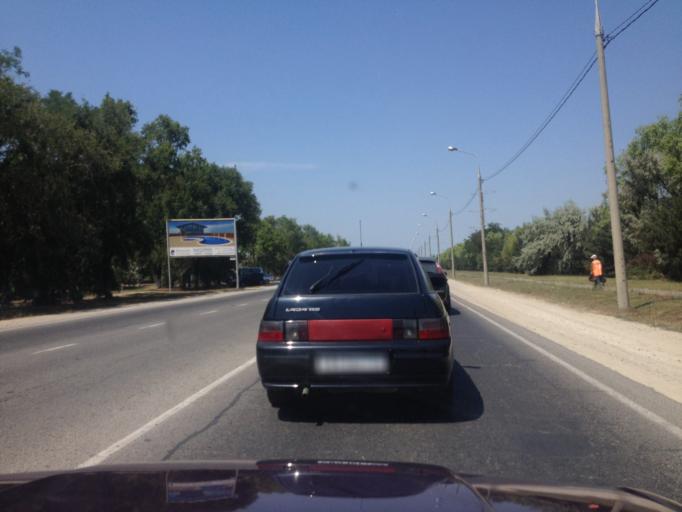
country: RU
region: Krasnodarskiy
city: Anapa
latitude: 44.9136
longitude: 37.3283
